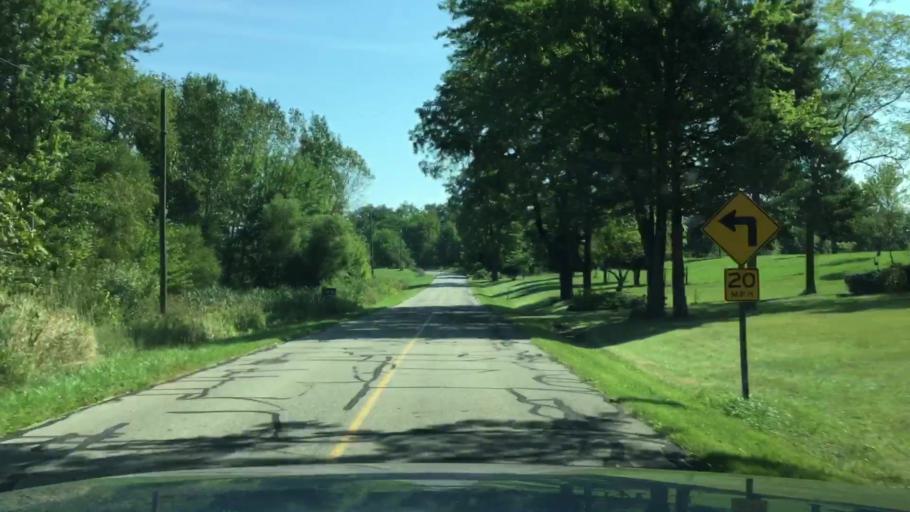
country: US
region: Michigan
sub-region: Lenawee County
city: Manitou Beach-Devils Lake
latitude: 42.0082
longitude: -84.3087
